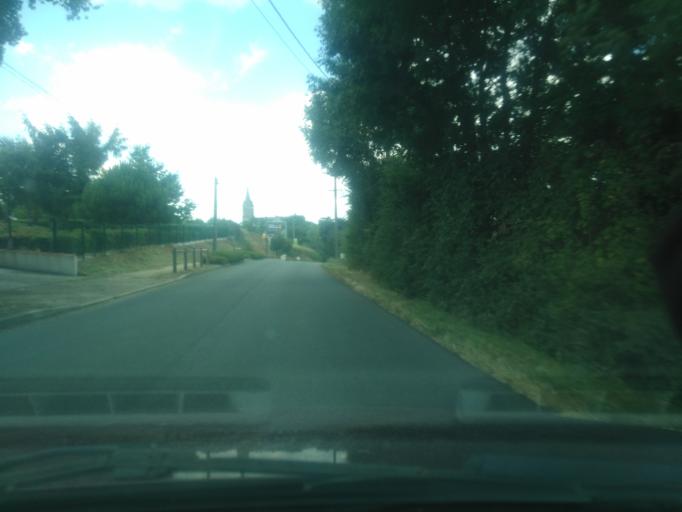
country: FR
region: Pays de la Loire
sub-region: Departement de la Vendee
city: Chauche
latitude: 46.8253
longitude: -1.2680
